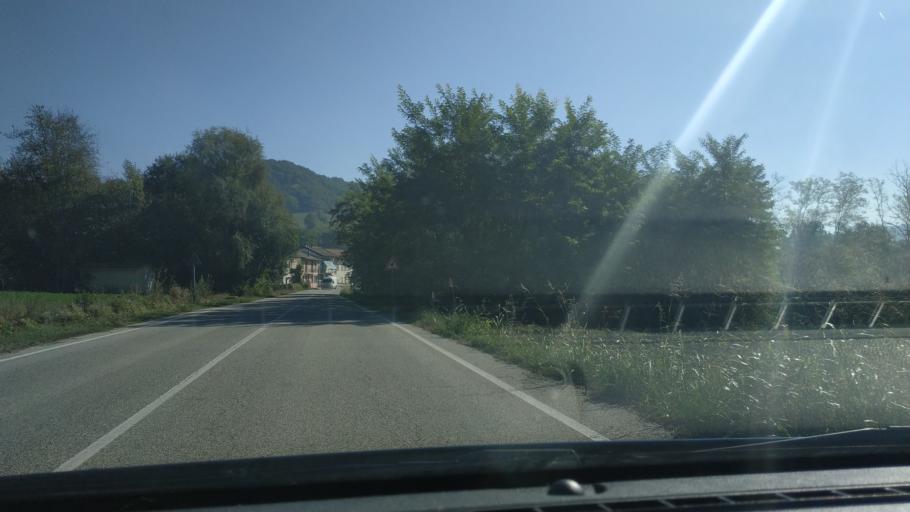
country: IT
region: Piedmont
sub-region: Provincia di Alessandria
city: Murisengo
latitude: 45.0920
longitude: 8.1386
